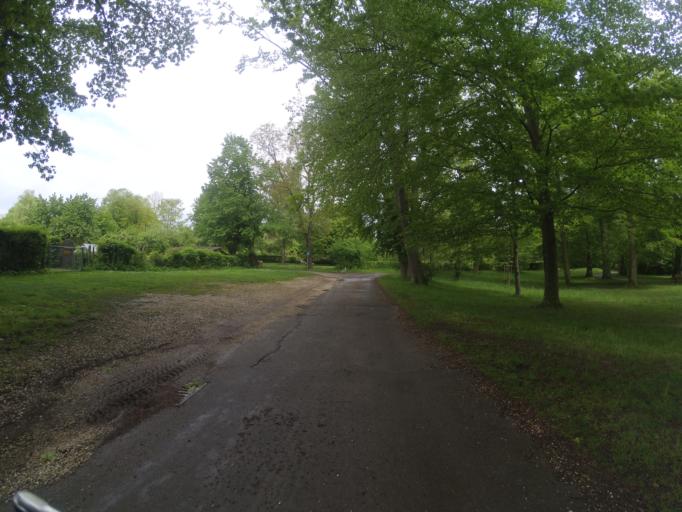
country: DE
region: Baden-Wuerttemberg
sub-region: Tuebingen Region
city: Ulm
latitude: 48.3828
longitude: 9.9672
